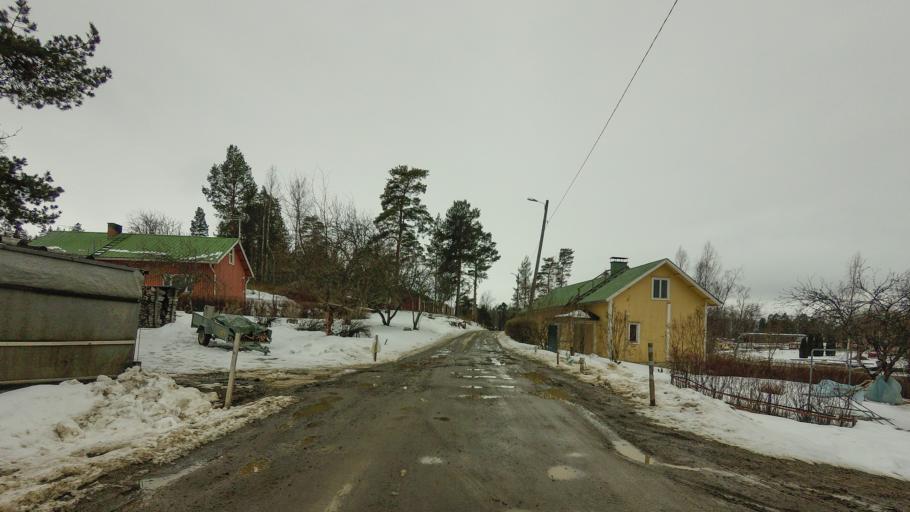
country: FI
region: Southern Savonia
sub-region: Savonlinna
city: Rantasalmi
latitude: 62.1149
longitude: 28.6089
